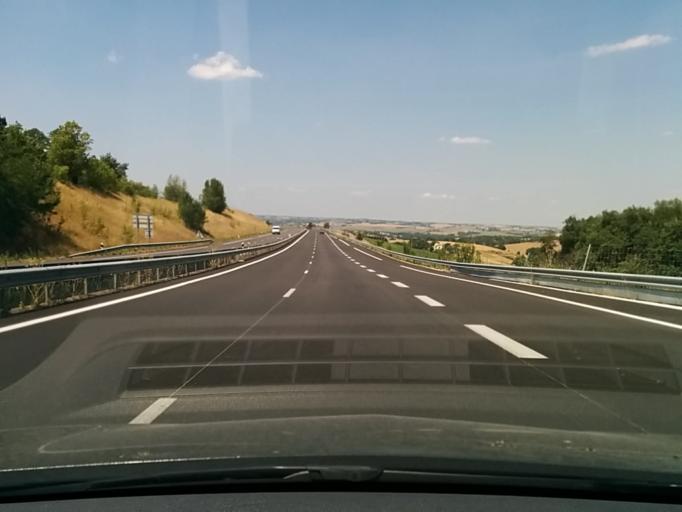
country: FR
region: Midi-Pyrenees
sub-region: Departement du Gers
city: Pujaudran
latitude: 43.5926
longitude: 1.1256
